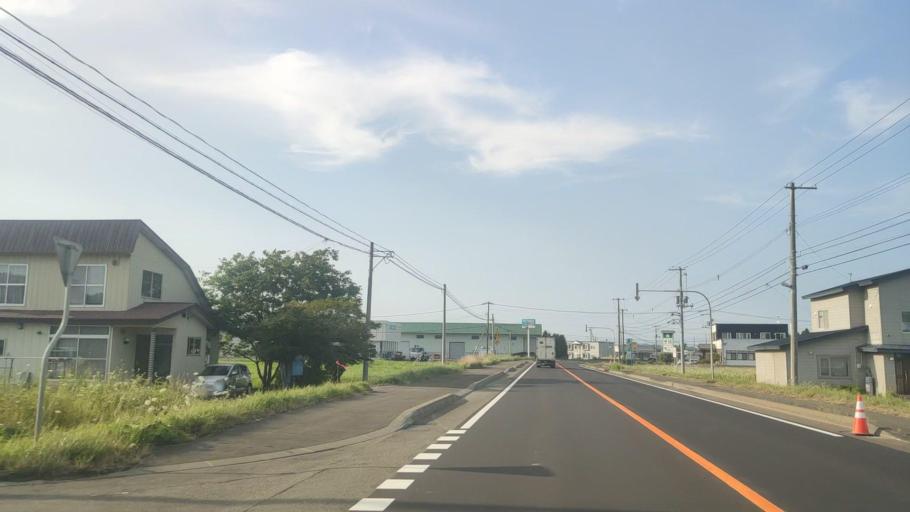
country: JP
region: Hokkaido
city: Iwamizawa
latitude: 43.0134
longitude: 141.7886
